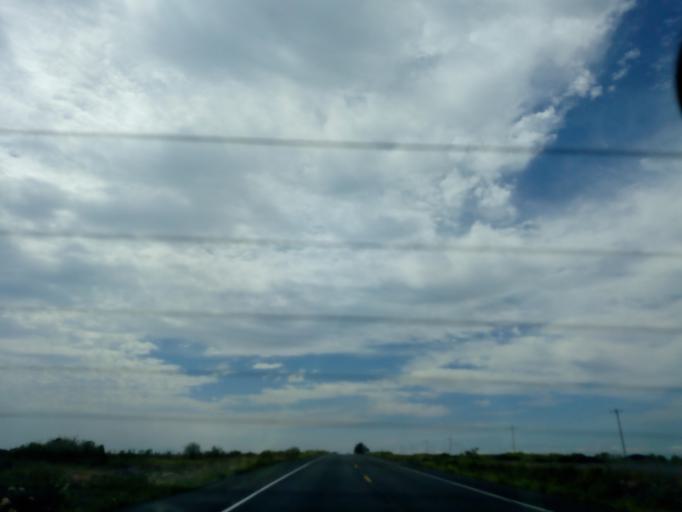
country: BR
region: Rio Grande do Sul
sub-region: Quarai
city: Quarai
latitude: -29.9757
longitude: -56.5512
